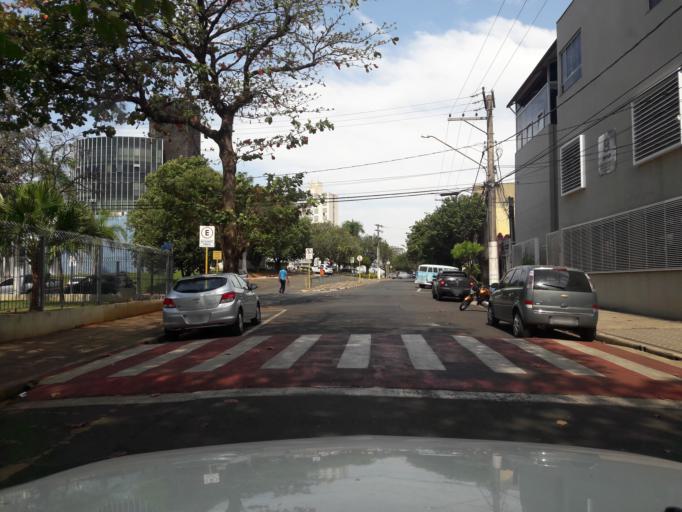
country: BR
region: Sao Paulo
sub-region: Moji-Guacu
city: Mogi-Gaucu
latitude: -22.3681
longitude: -46.9452
